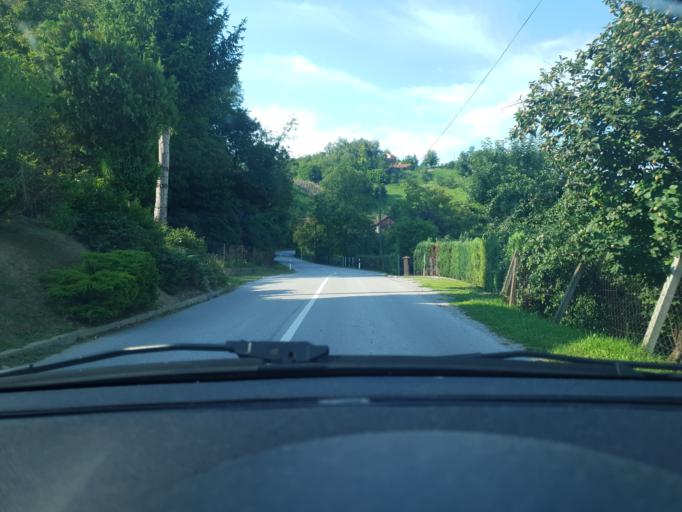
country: HR
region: Krapinsko-Zagorska
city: Pregrada
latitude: 46.0707
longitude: 15.7914
